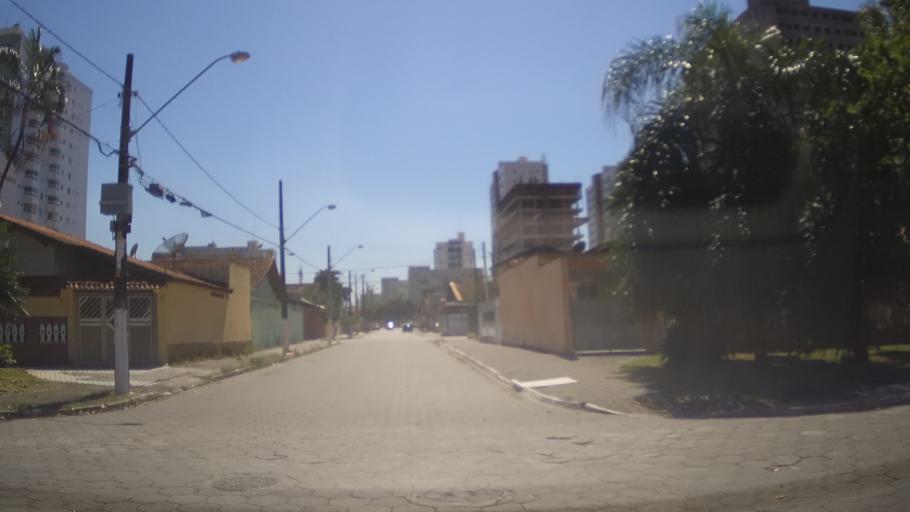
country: BR
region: Sao Paulo
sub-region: Praia Grande
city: Praia Grande
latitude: -24.0289
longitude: -46.4812
